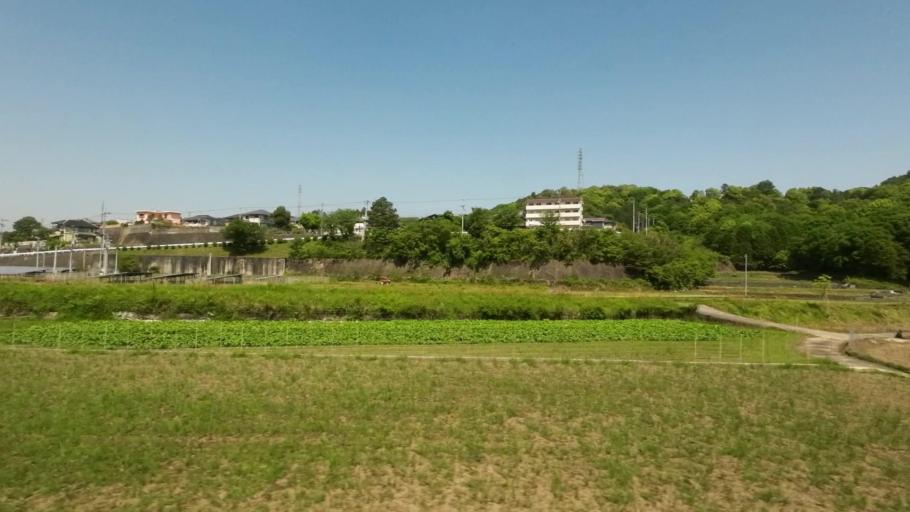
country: JP
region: Ehime
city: Niihama
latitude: 33.9313
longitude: 133.2709
